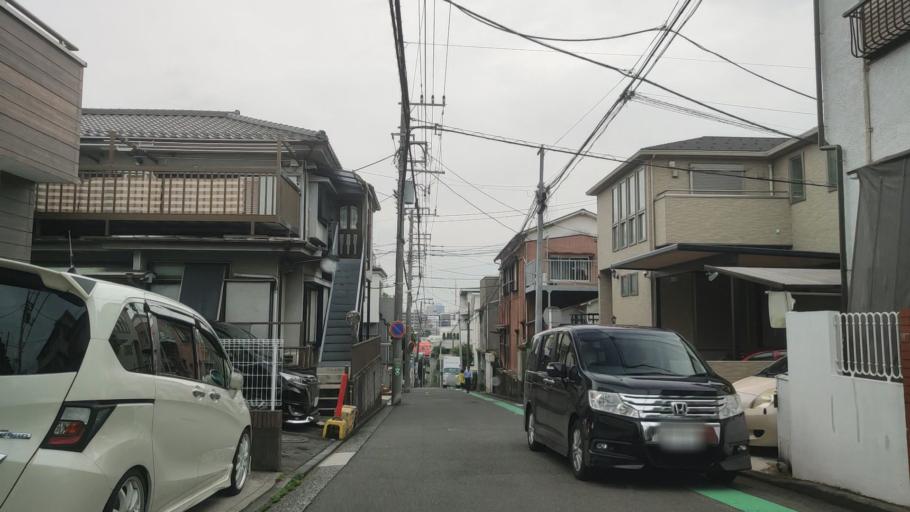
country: JP
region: Kanagawa
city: Yokohama
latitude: 35.4502
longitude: 139.6162
